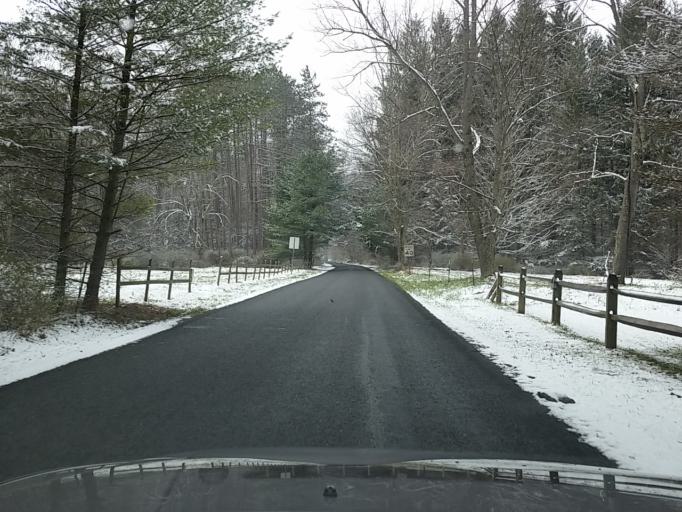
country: US
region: Pennsylvania
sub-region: Sullivan County
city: Laporte
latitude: 41.3057
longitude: -76.4248
